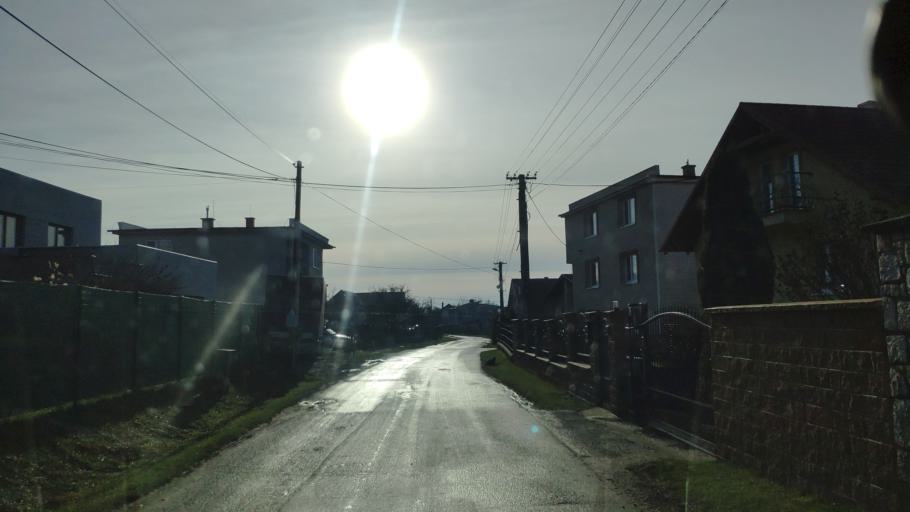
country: SK
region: Kosicky
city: Kosice
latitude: 48.6922
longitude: 21.3436
